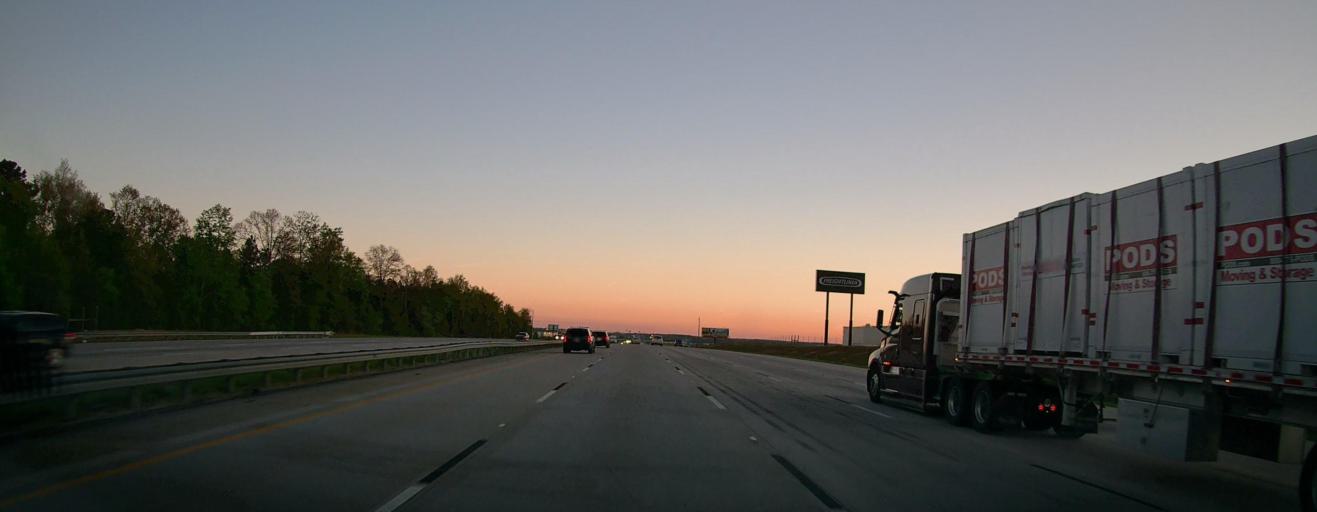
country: US
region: Georgia
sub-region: Peach County
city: Byron
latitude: 32.7381
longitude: -83.7190
